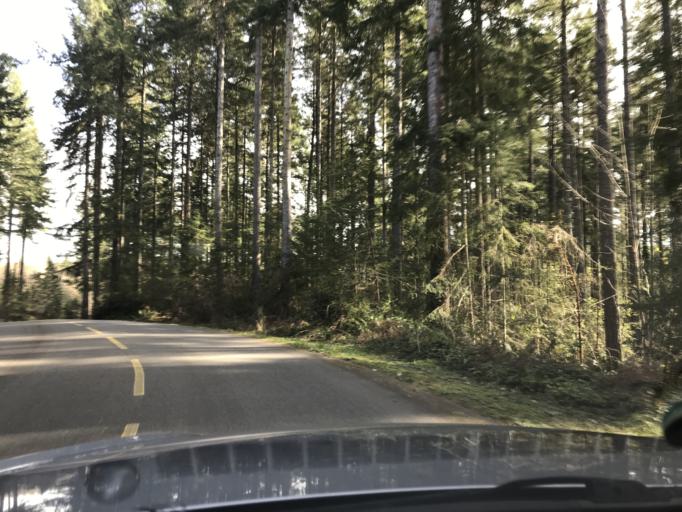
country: US
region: Washington
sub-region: Pierce County
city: Longbranch
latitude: 47.2250
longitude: -122.8061
